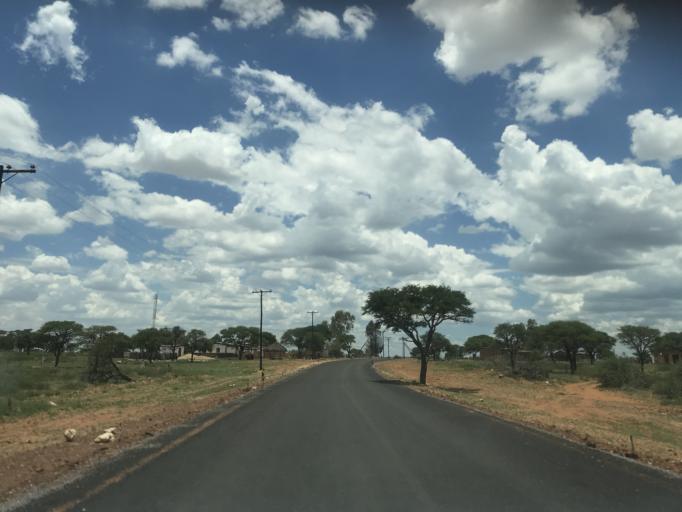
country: BW
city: Mabuli
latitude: -25.7893
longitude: 24.9006
